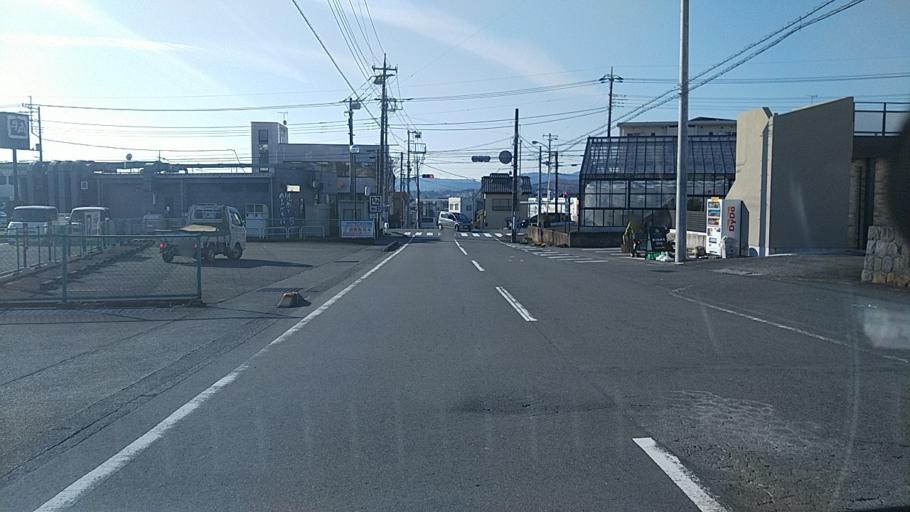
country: JP
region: Shizuoka
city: Fujinomiya
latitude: 35.2356
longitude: 138.6178
